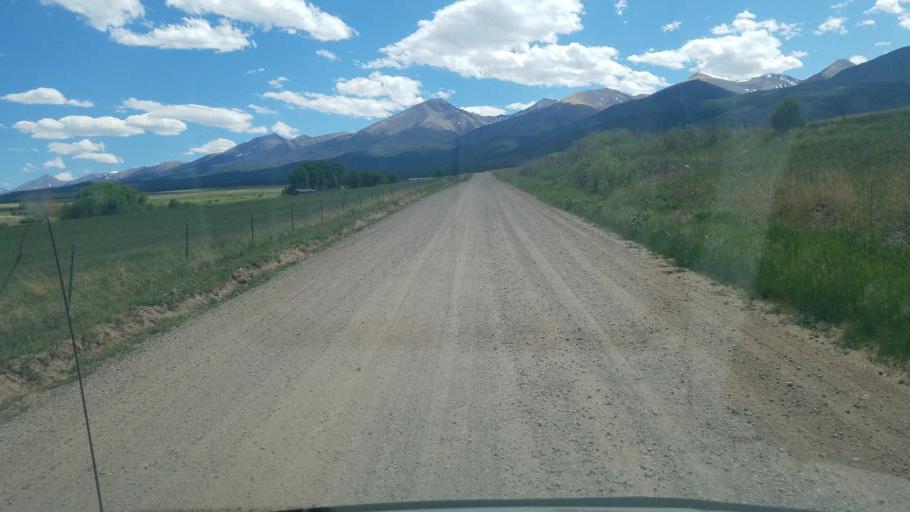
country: US
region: Colorado
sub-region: Custer County
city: Westcliffe
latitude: 38.2625
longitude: -105.6125
